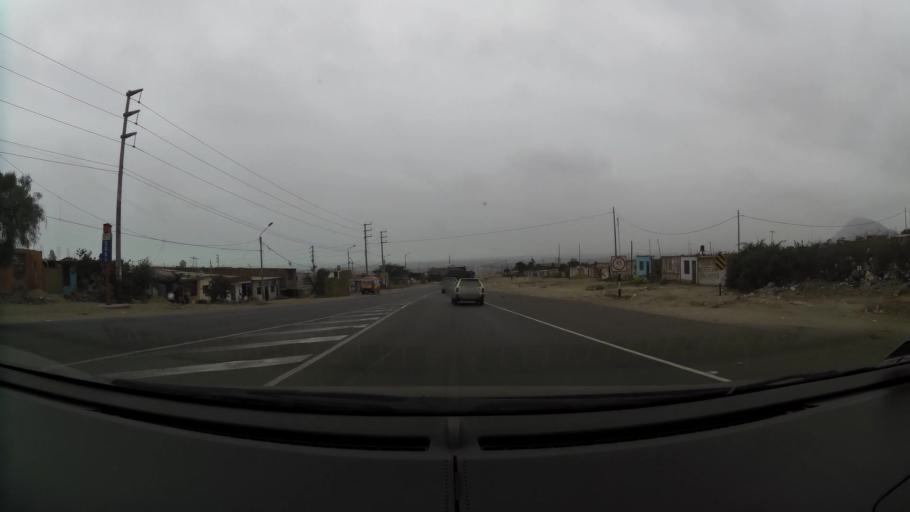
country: PE
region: La Libertad
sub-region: Provincia de Trujillo
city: Moche
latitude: -8.1858
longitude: -78.9828
